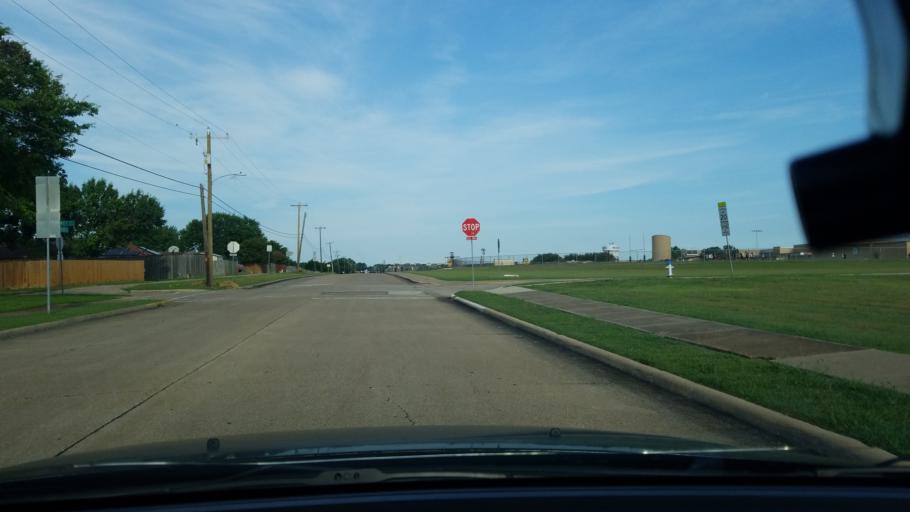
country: US
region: Texas
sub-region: Dallas County
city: Mesquite
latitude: 32.8050
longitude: -96.6053
